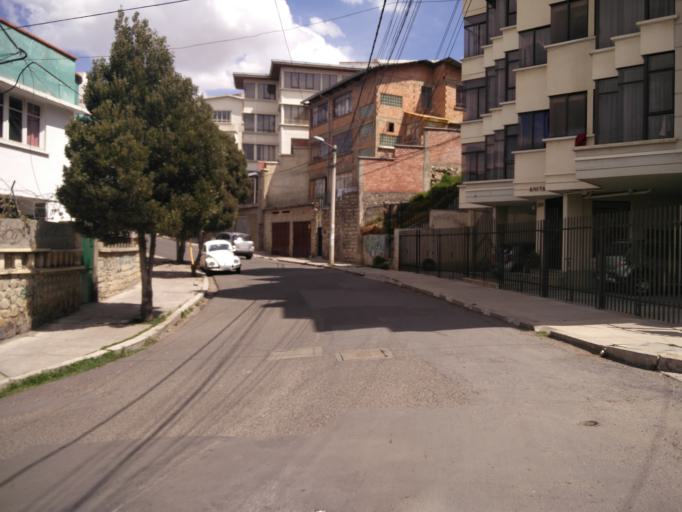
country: BO
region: La Paz
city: La Paz
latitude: -16.5095
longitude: -68.1337
